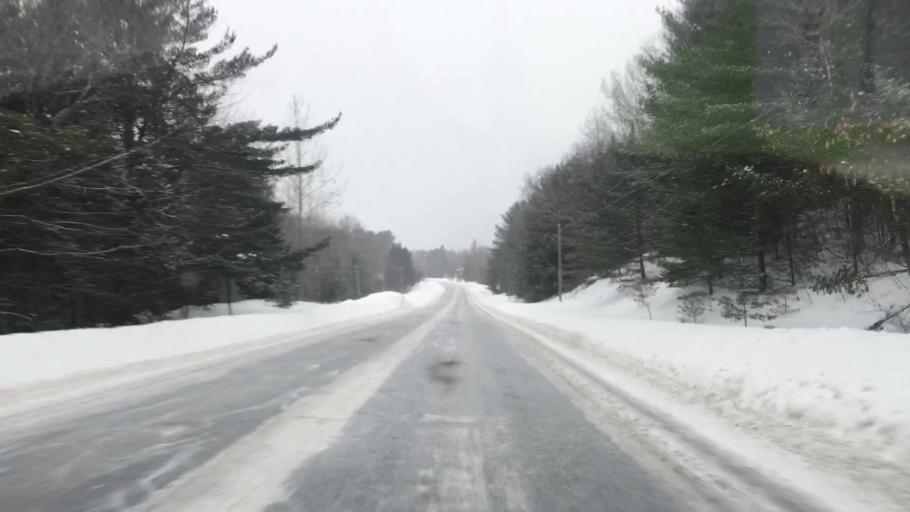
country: US
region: Maine
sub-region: Penobscot County
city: Medway
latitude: 45.5403
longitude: -68.3682
